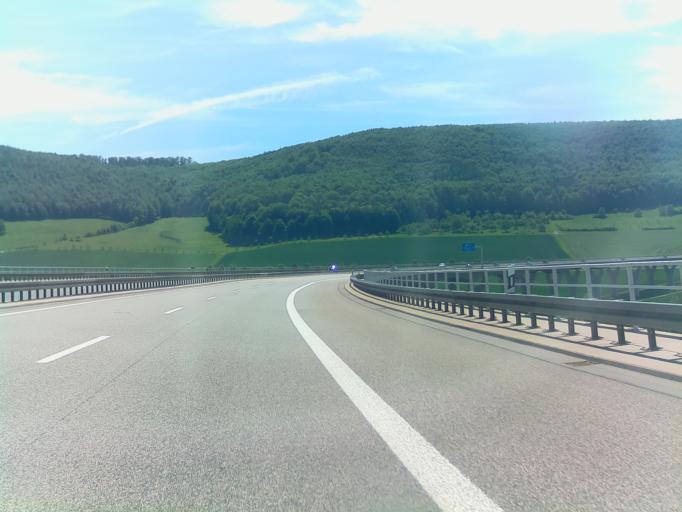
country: DE
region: Thuringia
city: Einhausen
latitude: 50.5322
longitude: 10.4761
